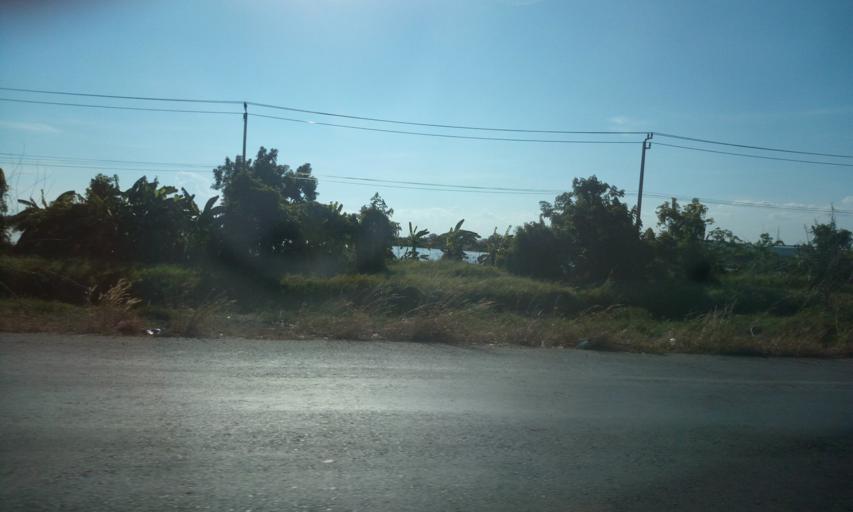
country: TH
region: Samut Prakan
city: Bang Bo District
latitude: 13.5673
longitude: 100.7555
